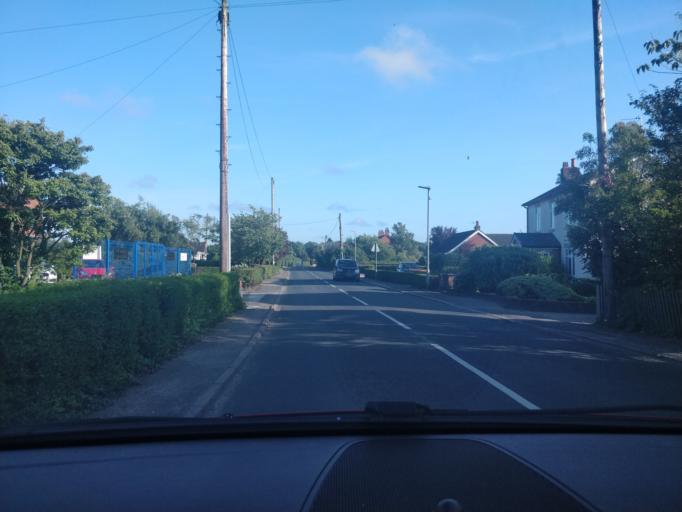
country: GB
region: England
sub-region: Lancashire
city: Banks
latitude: 53.6617
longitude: -2.8795
